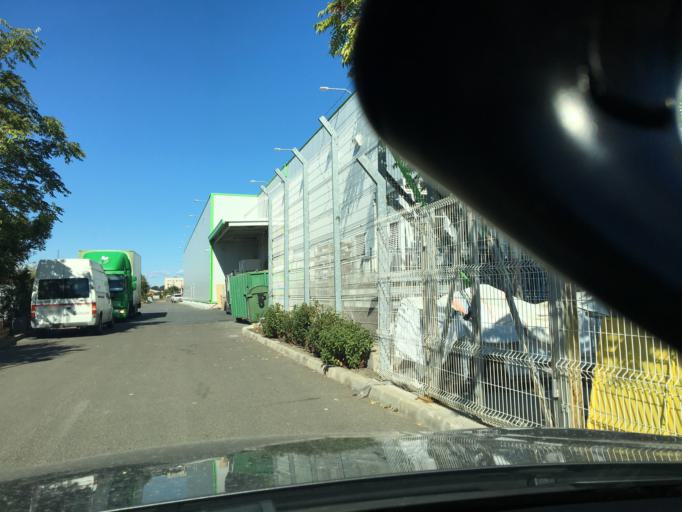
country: BG
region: Burgas
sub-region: Obshtina Burgas
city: Burgas
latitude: 42.5131
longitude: 27.4517
